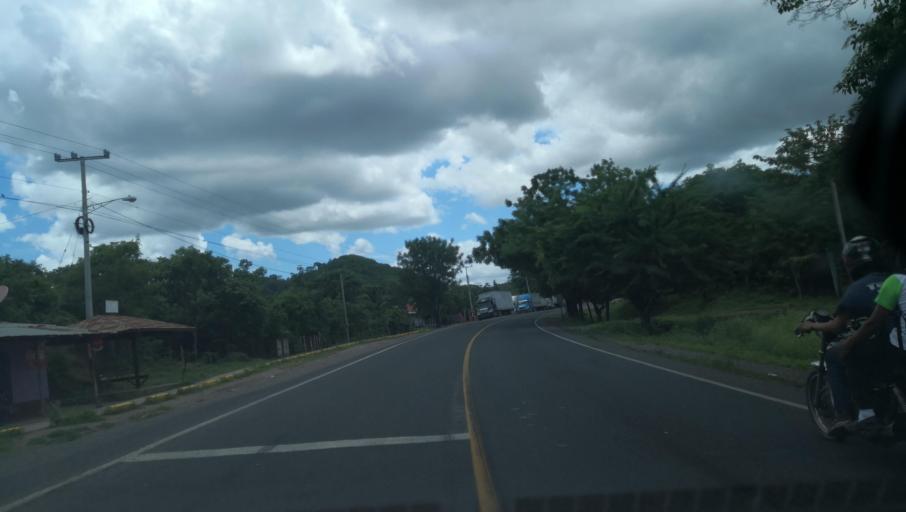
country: NI
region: Madriz
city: Palacaguina
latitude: 13.4537
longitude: -86.4498
